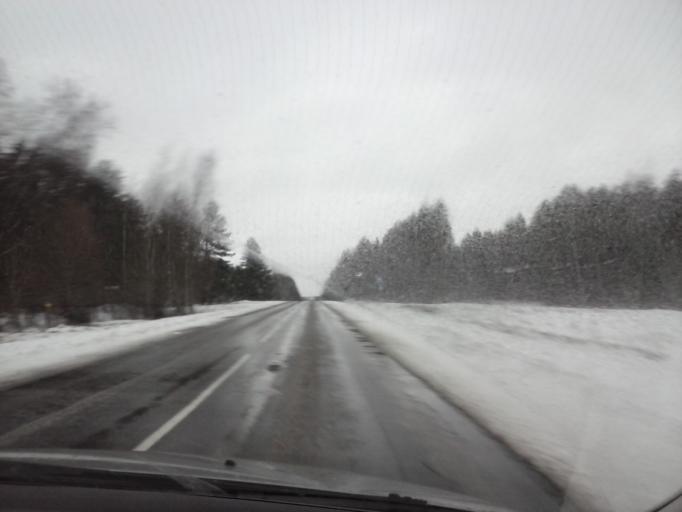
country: LV
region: Valkas Rajons
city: Valka
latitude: 57.7276
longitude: 25.9380
